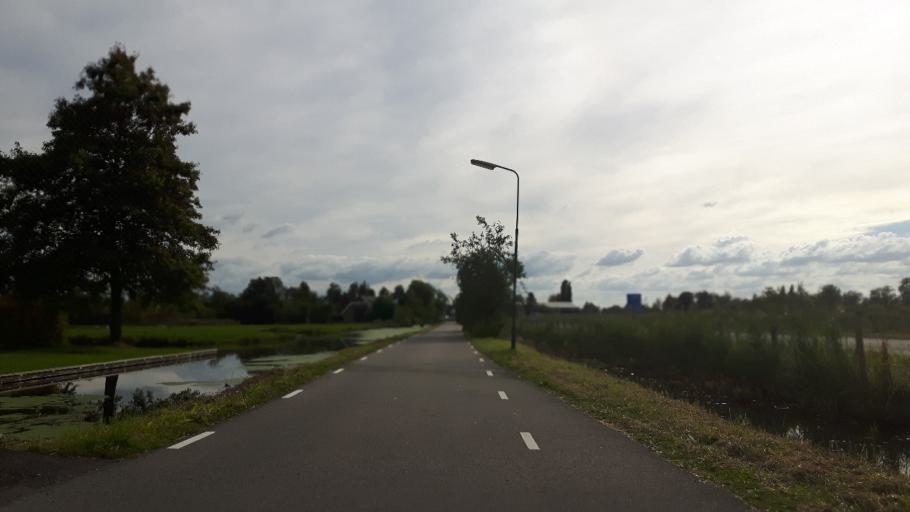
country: NL
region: Utrecht
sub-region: Gemeente De Ronde Venen
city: Mijdrecht
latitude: 52.1580
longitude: 4.8562
